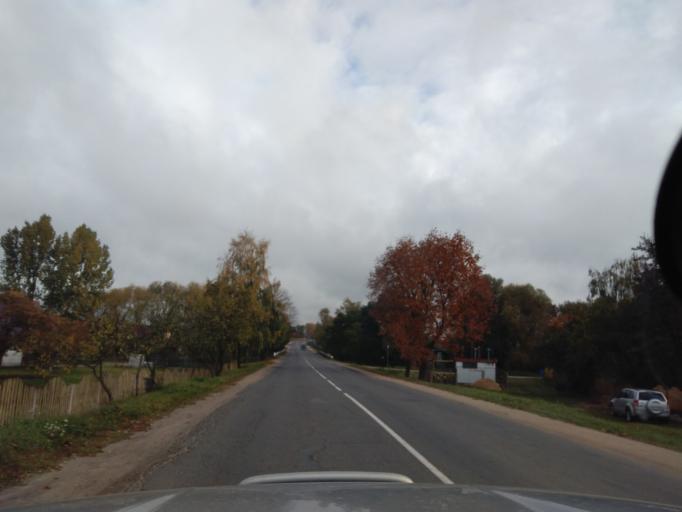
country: BY
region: Minsk
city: Kapyl'
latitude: 53.1558
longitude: 27.0760
